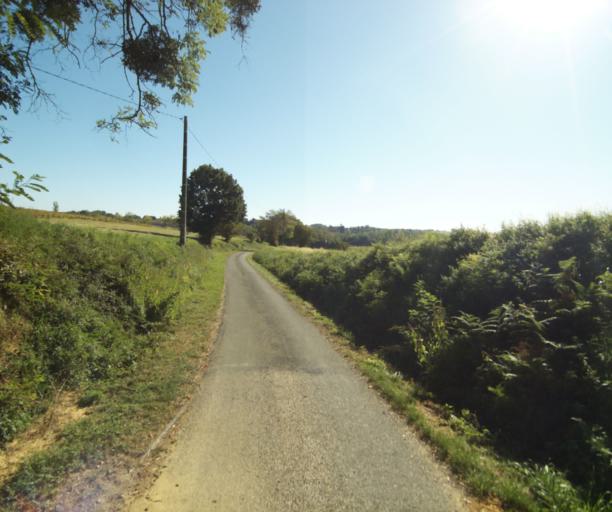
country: FR
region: Midi-Pyrenees
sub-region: Departement du Gers
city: Eauze
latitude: 43.8081
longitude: 0.1730
